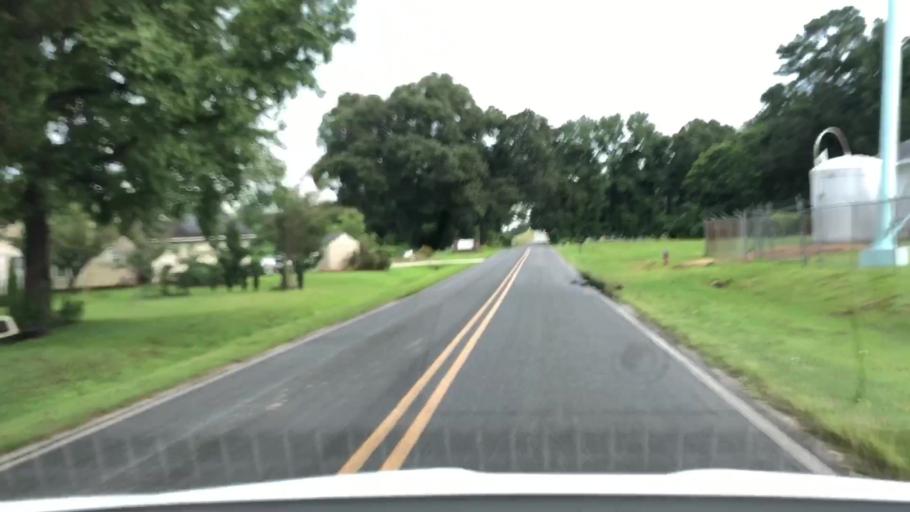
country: US
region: North Carolina
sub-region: Jones County
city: Maysville
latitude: 34.9069
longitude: -77.2330
